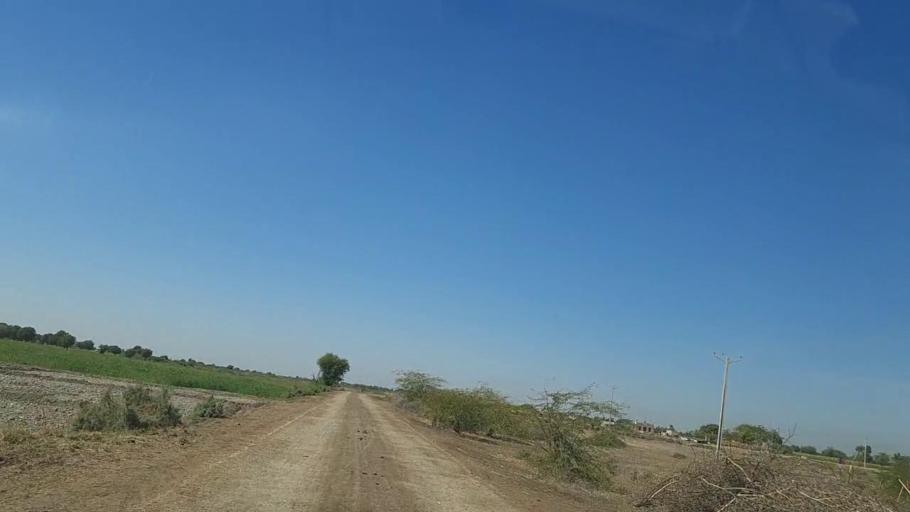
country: PK
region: Sindh
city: Dhoro Naro
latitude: 25.4892
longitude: 69.5115
